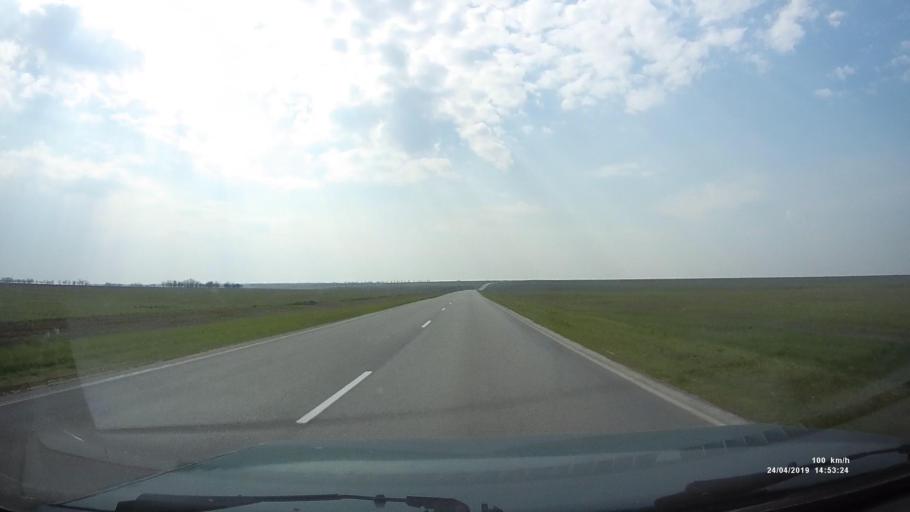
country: RU
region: Rostov
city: Remontnoye
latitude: 46.5313
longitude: 43.6596
